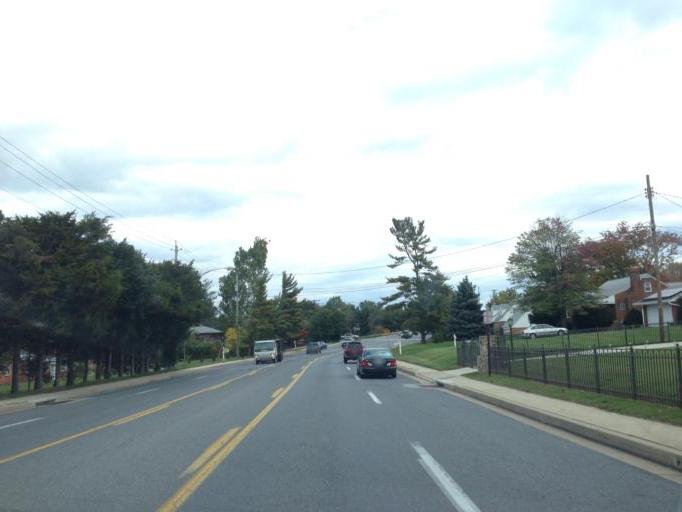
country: US
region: Maryland
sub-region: Baltimore County
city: Milford Mill
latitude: 39.3685
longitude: -76.7511
